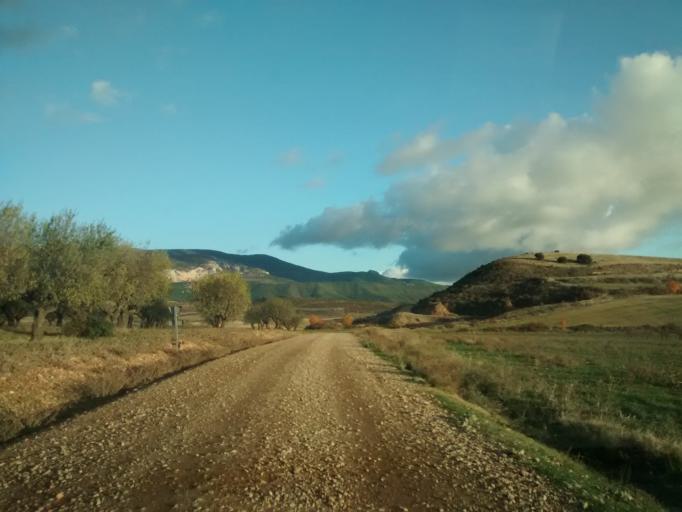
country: ES
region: Aragon
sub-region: Provincia de Huesca
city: Loarre
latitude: 42.3120
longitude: -0.6164
